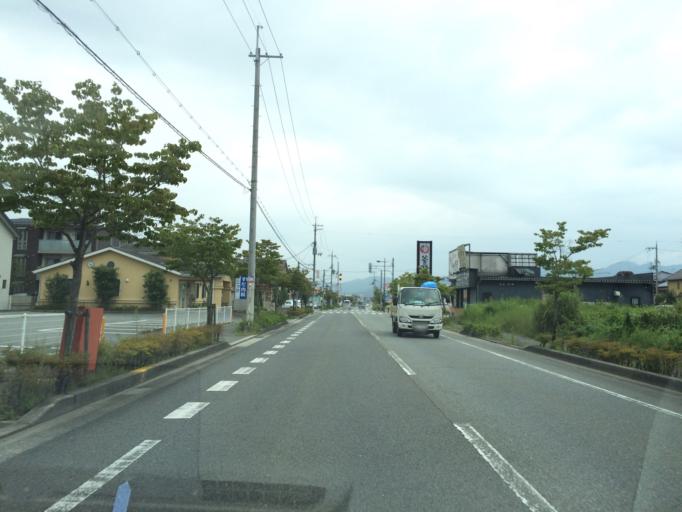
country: JP
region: Hyogo
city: Toyooka
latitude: 35.5364
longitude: 134.8087
